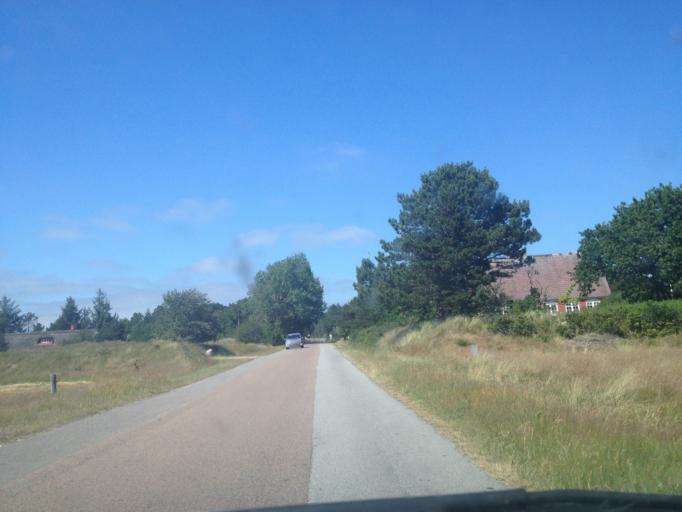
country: DE
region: Schleswig-Holstein
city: List
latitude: 55.0908
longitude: 8.5429
